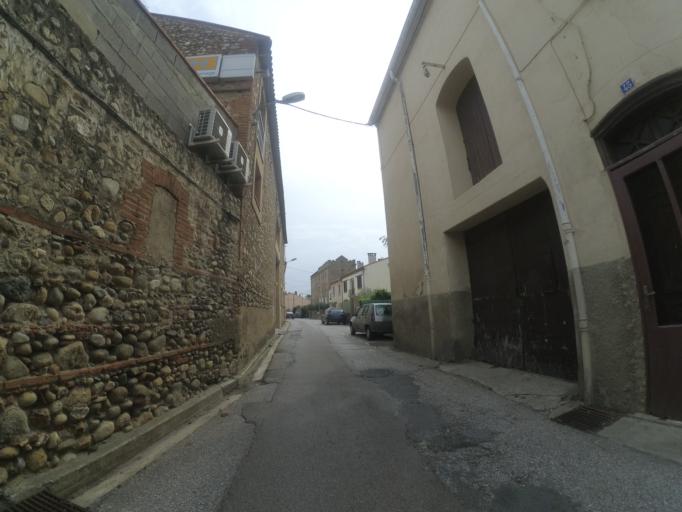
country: FR
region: Languedoc-Roussillon
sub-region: Departement des Pyrenees-Orientales
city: Millas
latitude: 42.6908
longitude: 2.6944
